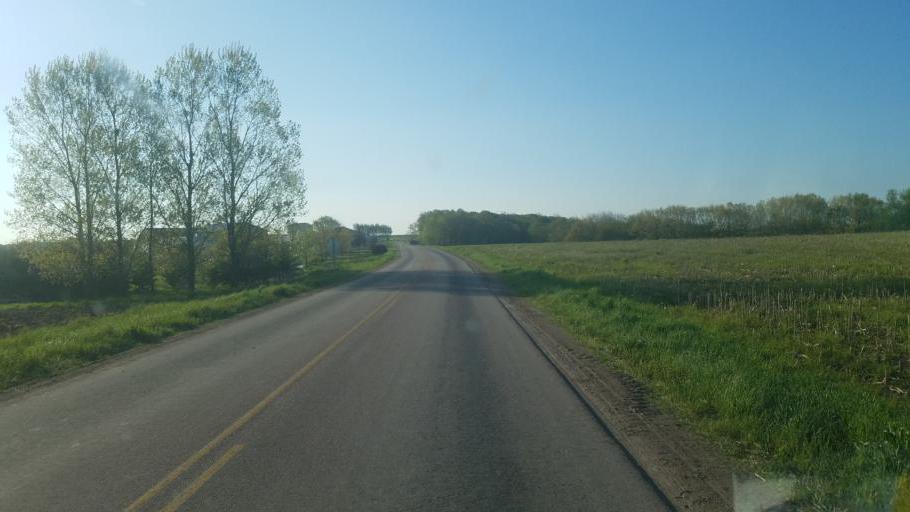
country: US
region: Wisconsin
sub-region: Vernon County
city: Hillsboro
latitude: 43.6150
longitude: -90.4463
